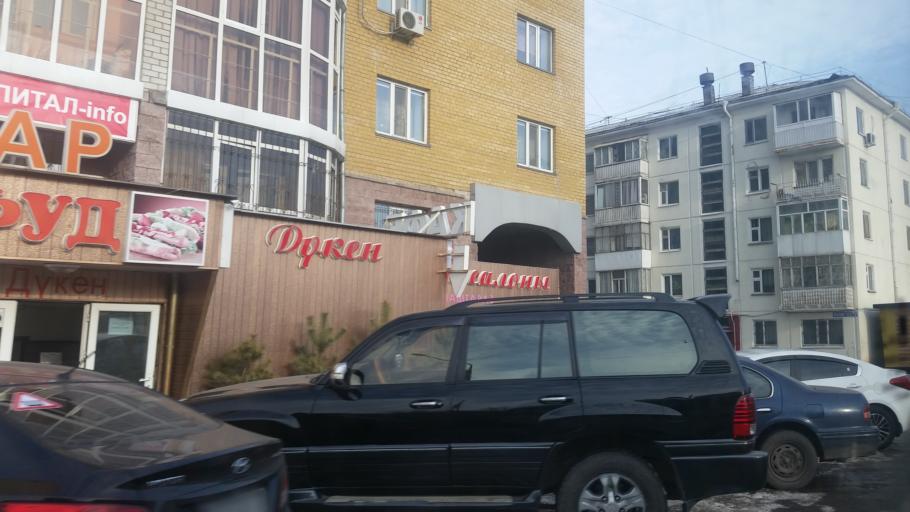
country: KZ
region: Astana Qalasy
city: Astana
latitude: 51.1878
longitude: 71.4057
